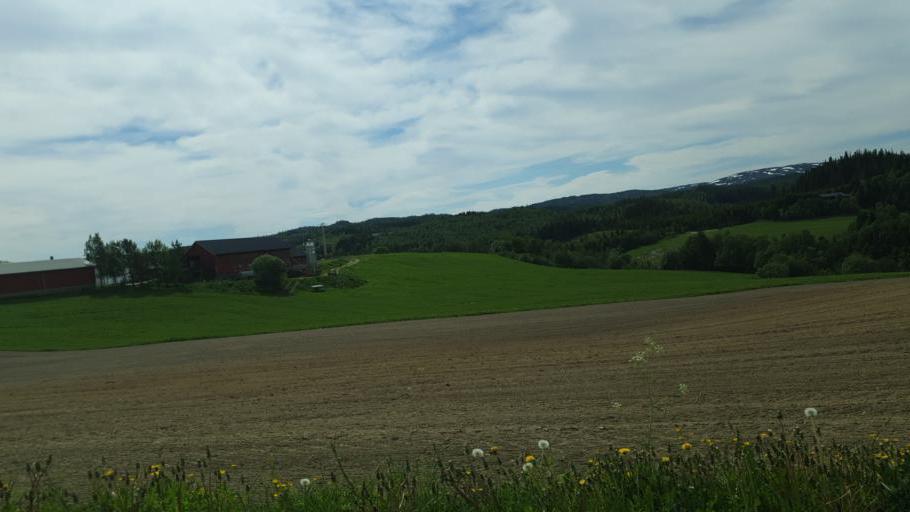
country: NO
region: Nord-Trondelag
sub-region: Leksvik
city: Leksvik
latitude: 63.6845
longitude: 10.5765
